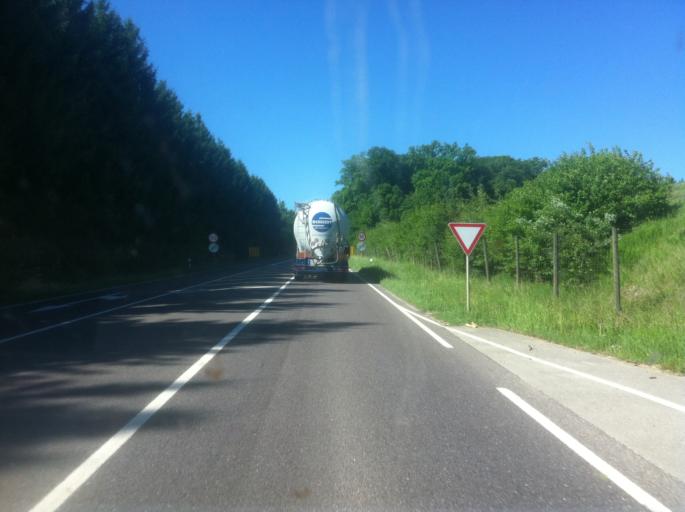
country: LU
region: Grevenmacher
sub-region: Canton d'Echternach
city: Bech
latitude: 49.7694
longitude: 6.3718
